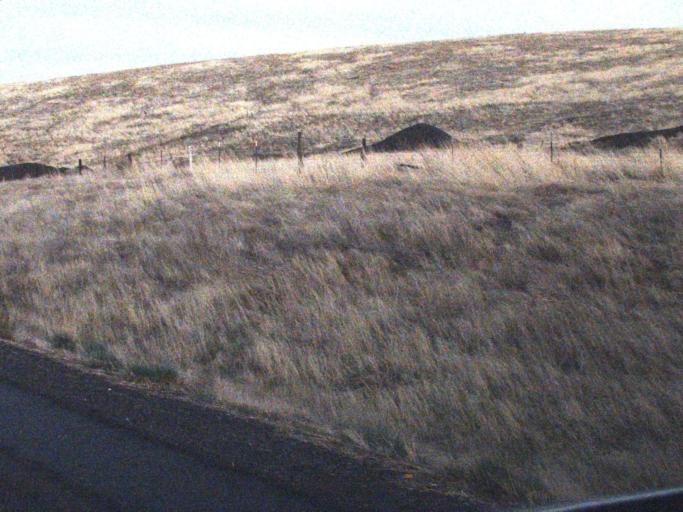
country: US
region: Washington
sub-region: Columbia County
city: Dayton
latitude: 46.5412
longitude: -117.8982
